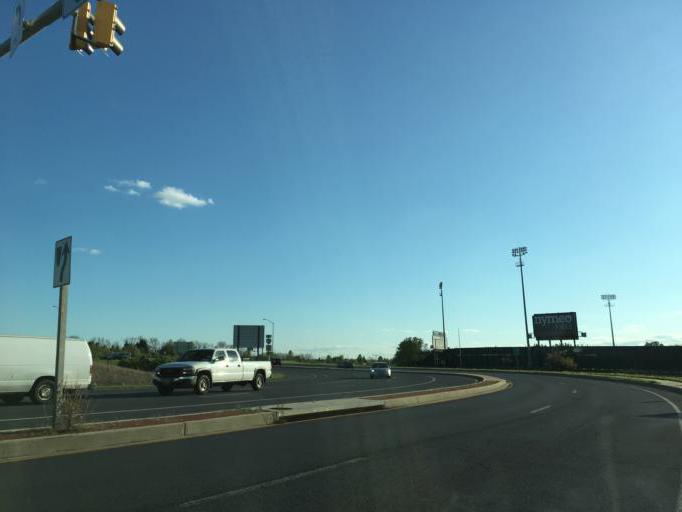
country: US
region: Maryland
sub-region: Frederick County
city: Frederick
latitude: 39.4025
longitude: -77.4107
